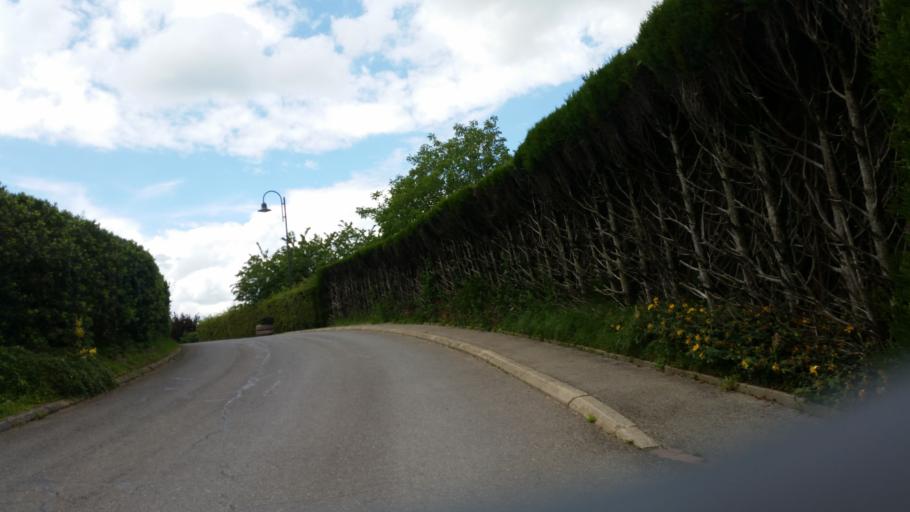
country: CH
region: Vaud
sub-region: Lausanne District
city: Cheseaux
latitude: 46.5998
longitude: 6.6170
